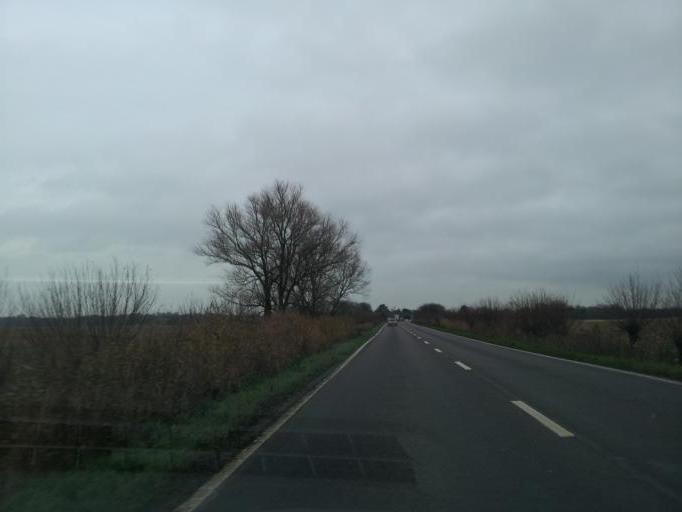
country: GB
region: England
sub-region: Norfolk
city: Acle
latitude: 52.6566
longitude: 1.5788
